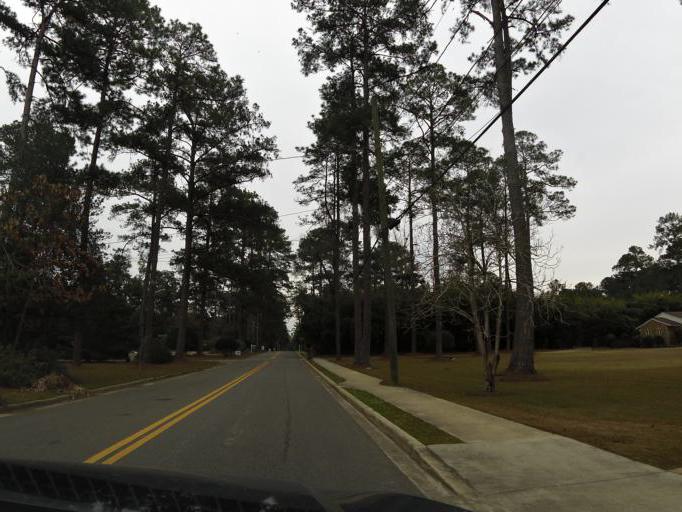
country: US
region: Georgia
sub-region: Thomas County
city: Thomasville
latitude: 30.8225
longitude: -83.9703
